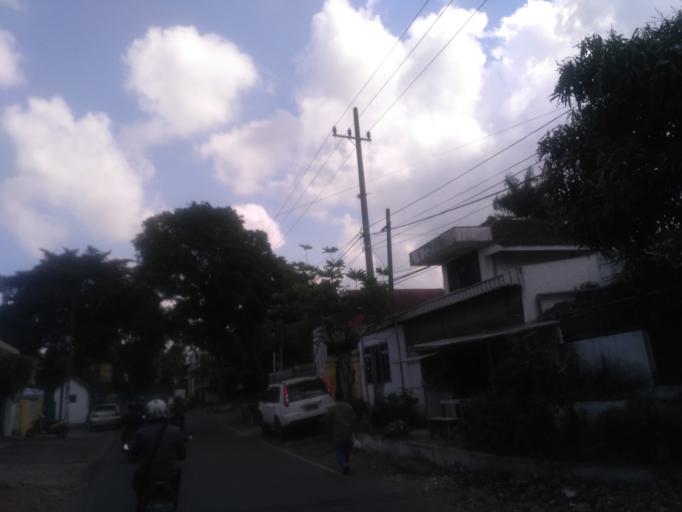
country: ID
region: East Java
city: Malang
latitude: -7.9424
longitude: 112.6309
